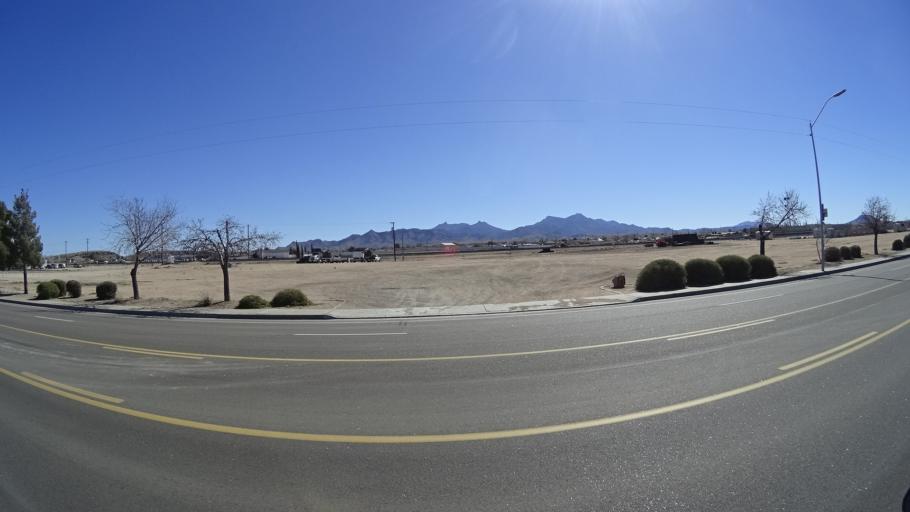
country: US
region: Arizona
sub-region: Mohave County
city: Kingman
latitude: 35.2058
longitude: -114.0205
